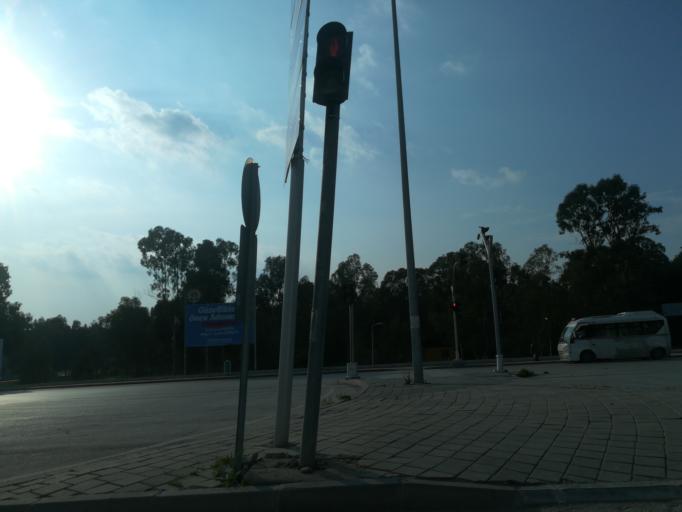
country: TR
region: Adana
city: Adana
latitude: 37.0298
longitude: 35.3455
